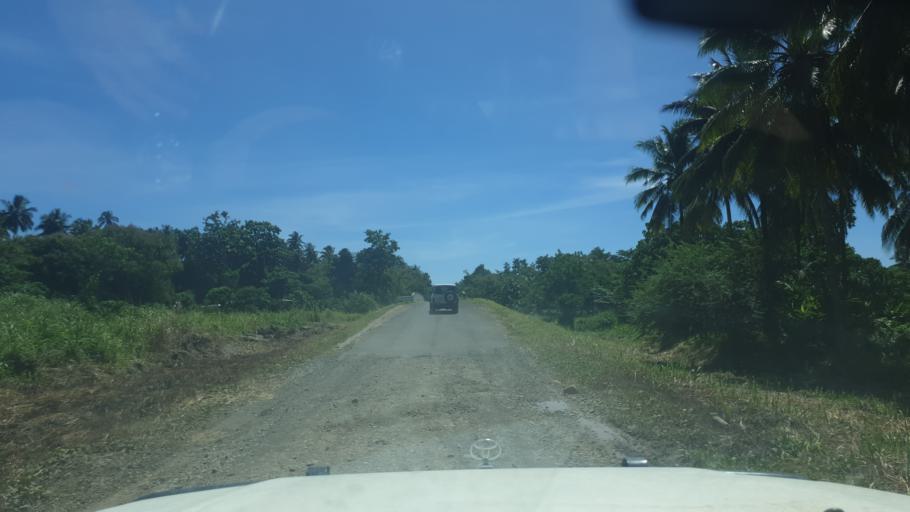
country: PG
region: Bougainville
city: Buka
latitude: -5.6609
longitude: 155.0968
